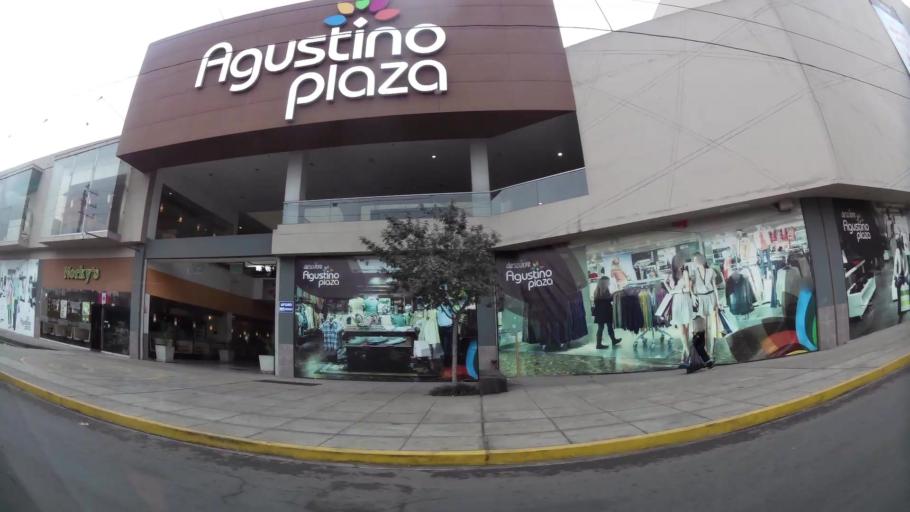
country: PE
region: Lima
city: Lima
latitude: -12.0413
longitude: -77.0030
